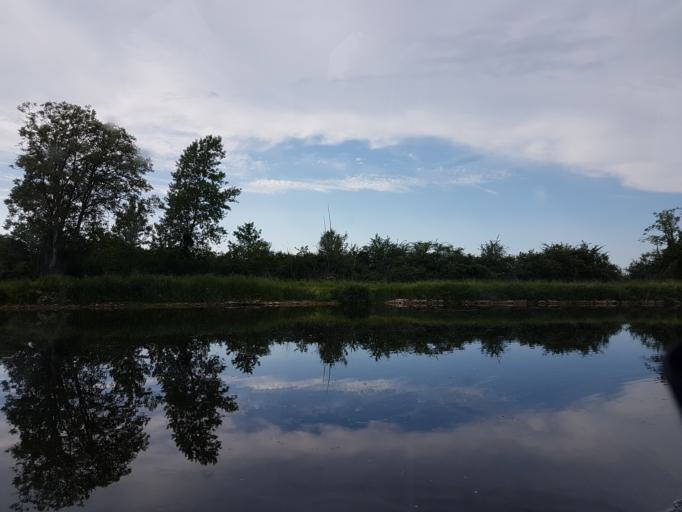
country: FR
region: Bourgogne
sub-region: Departement de l'Yonne
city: Moneteau
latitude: 47.8396
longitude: 3.5742
